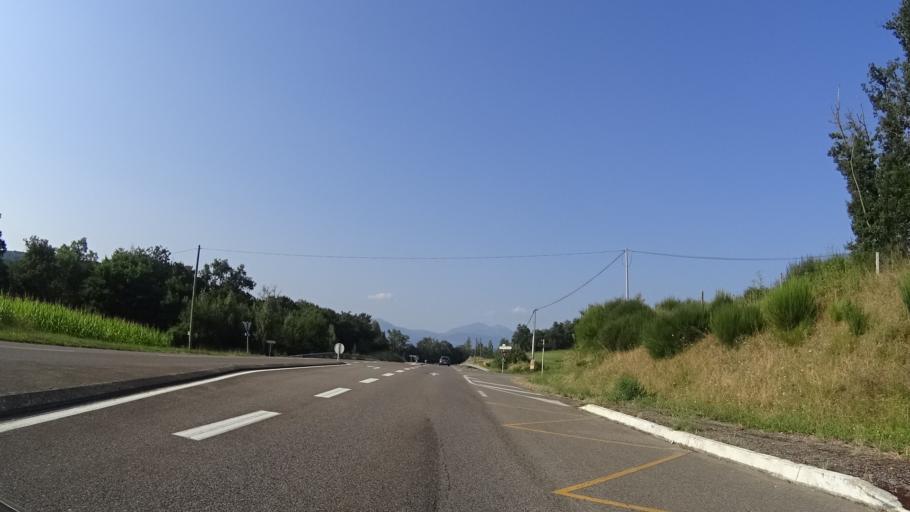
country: FR
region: Midi-Pyrenees
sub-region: Departement de l'Ariege
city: Mirepoix
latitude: 43.0169
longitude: 1.8908
